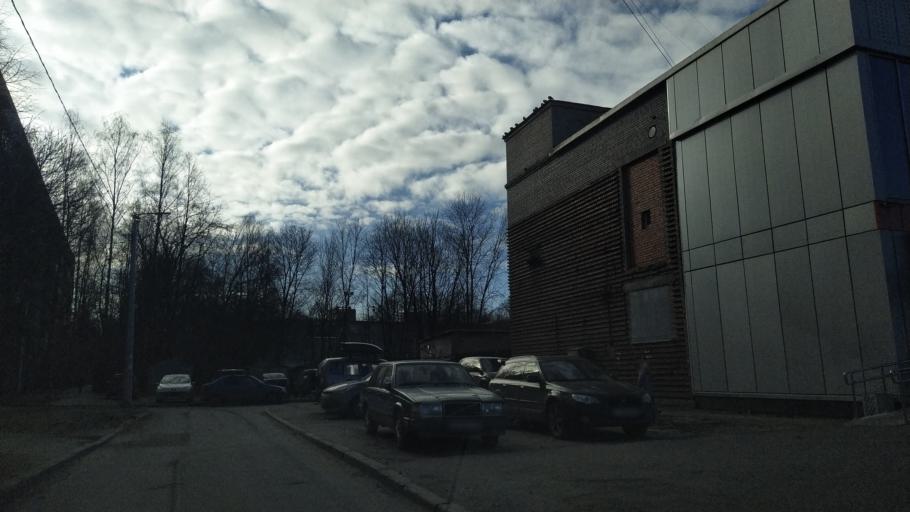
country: RU
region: Leningrad
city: Akademicheskoe
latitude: 60.0078
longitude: 30.3994
